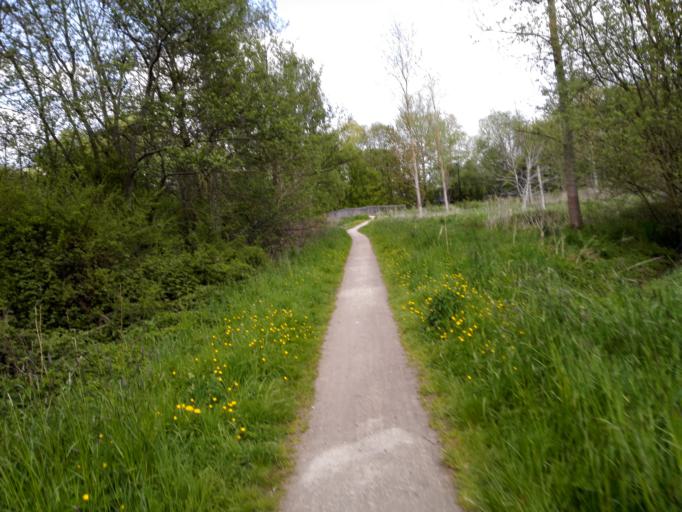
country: BE
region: Flanders
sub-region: Provincie Vlaams-Brabant
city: Rotselaar
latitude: 50.9597
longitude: 4.7228
